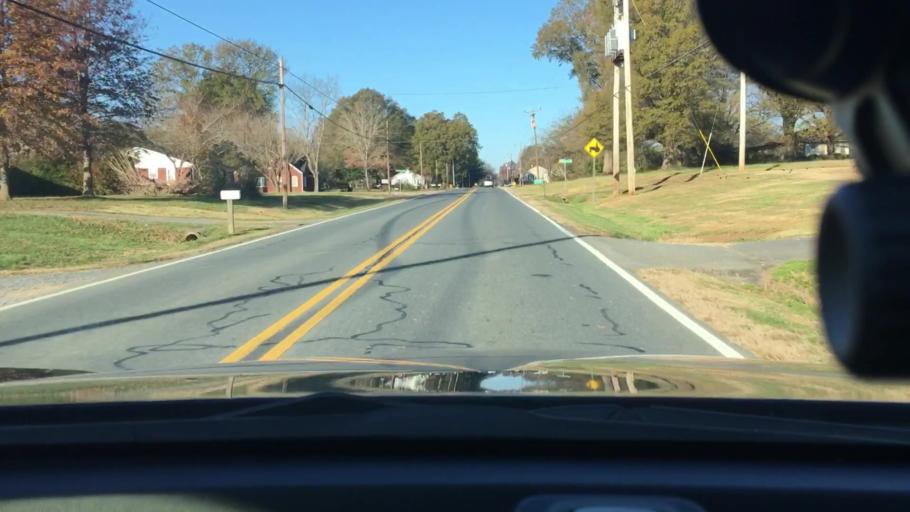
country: US
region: North Carolina
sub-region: Stanly County
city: Albemarle
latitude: 35.3697
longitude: -80.2756
